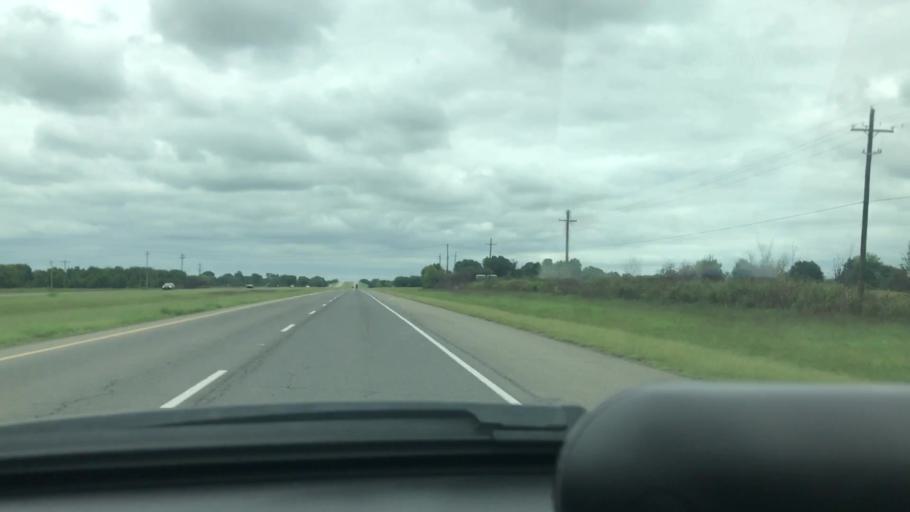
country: US
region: Oklahoma
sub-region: Wagoner County
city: Wagoner
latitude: 35.8643
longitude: -95.4025
